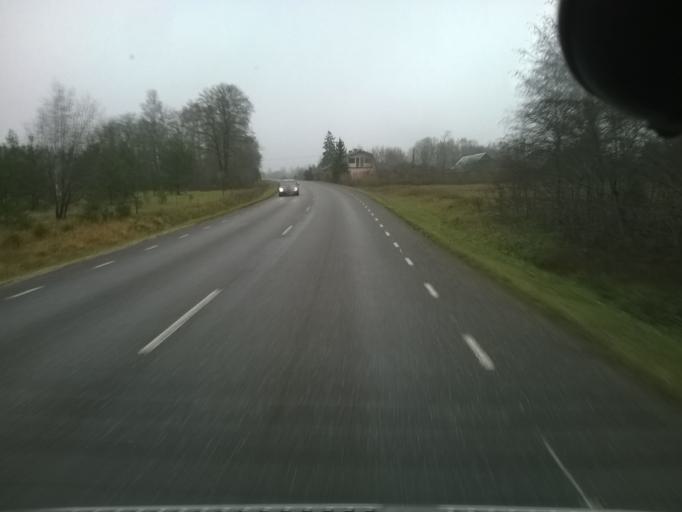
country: EE
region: Raplamaa
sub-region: Kohila vald
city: Kohila
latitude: 59.1553
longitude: 24.6282
